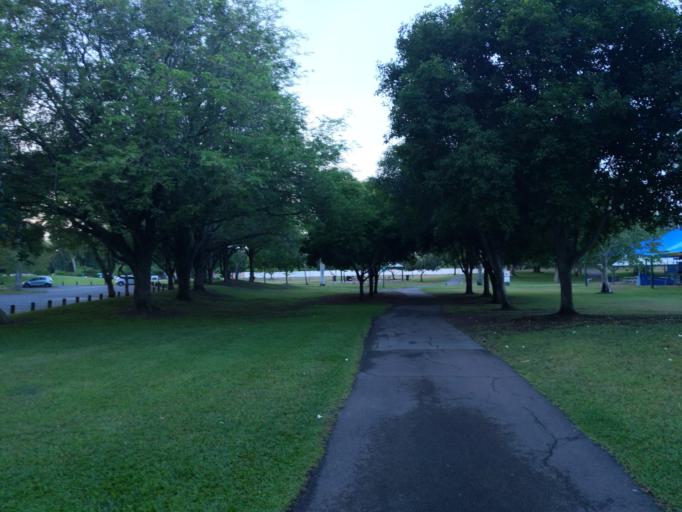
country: AU
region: Northern Territory
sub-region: Darwin
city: Nightcliff
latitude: -12.3866
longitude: 130.8681
